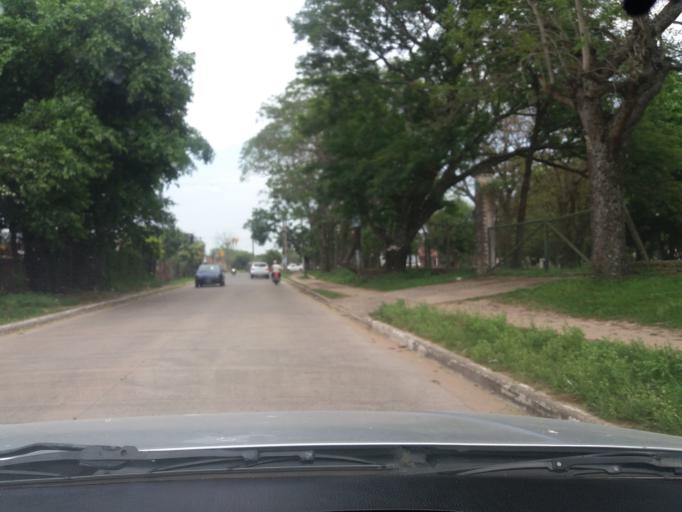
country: AR
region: Corrientes
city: Corrientes
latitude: -27.5135
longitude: -58.8064
